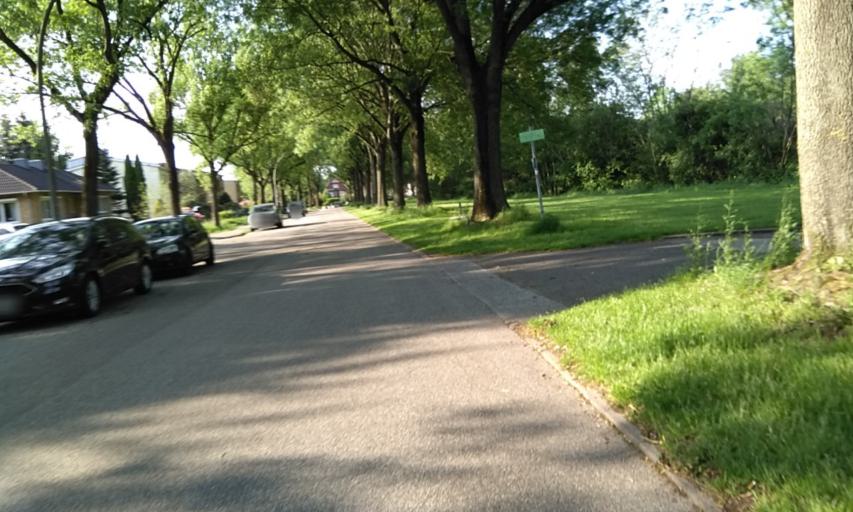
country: DE
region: Hamburg
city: Altona
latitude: 53.5304
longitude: 9.8637
